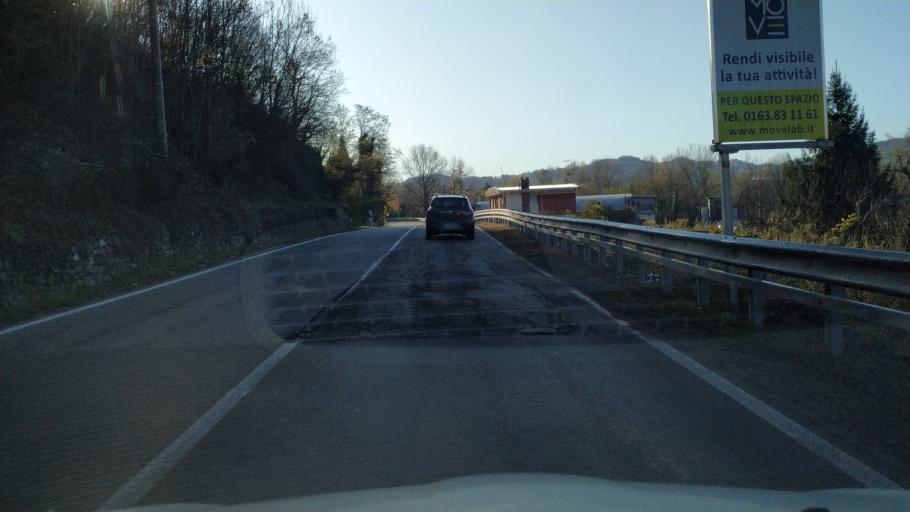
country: IT
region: Piedmont
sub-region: Provincia di Vercelli
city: Serravalle Sesia
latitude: 45.6867
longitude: 8.3260
